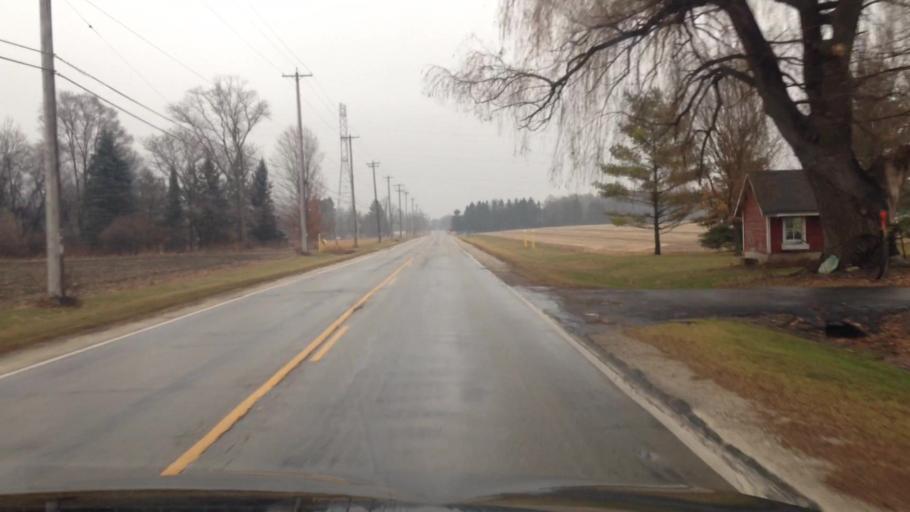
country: US
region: Wisconsin
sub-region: Washington County
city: Richfield
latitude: 43.2502
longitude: -88.1565
